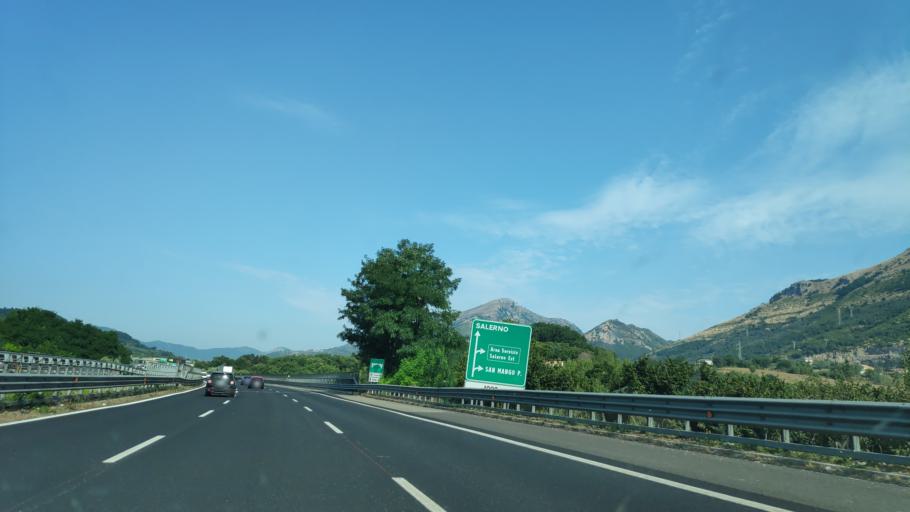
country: IT
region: Campania
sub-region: Provincia di Salerno
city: San Mango Piemonte
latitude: 40.6852
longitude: 14.8525
